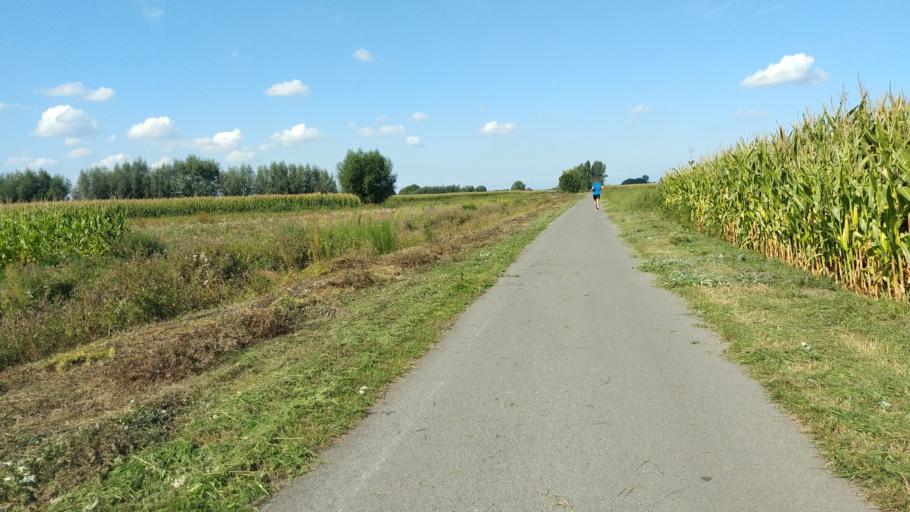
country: BE
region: Flanders
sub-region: Provincie Oost-Vlaanderen
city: Assenede
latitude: 51.2298
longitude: 3.7408
